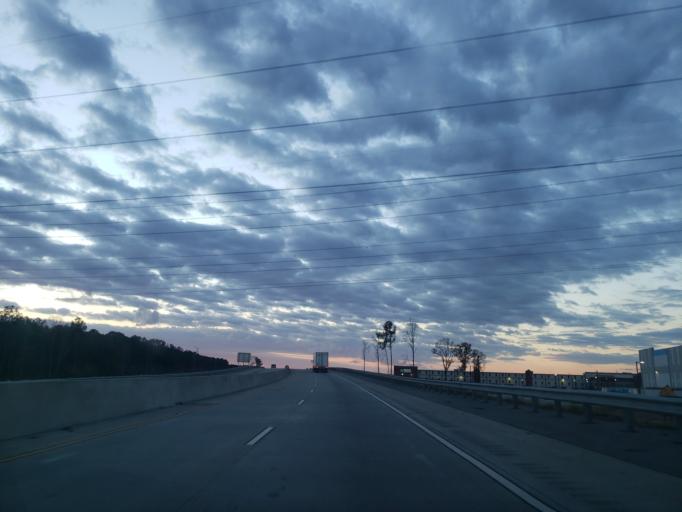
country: US
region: Georgia
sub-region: Chatham County
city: Port Wentworth
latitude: 32.1493
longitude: -81.1747
